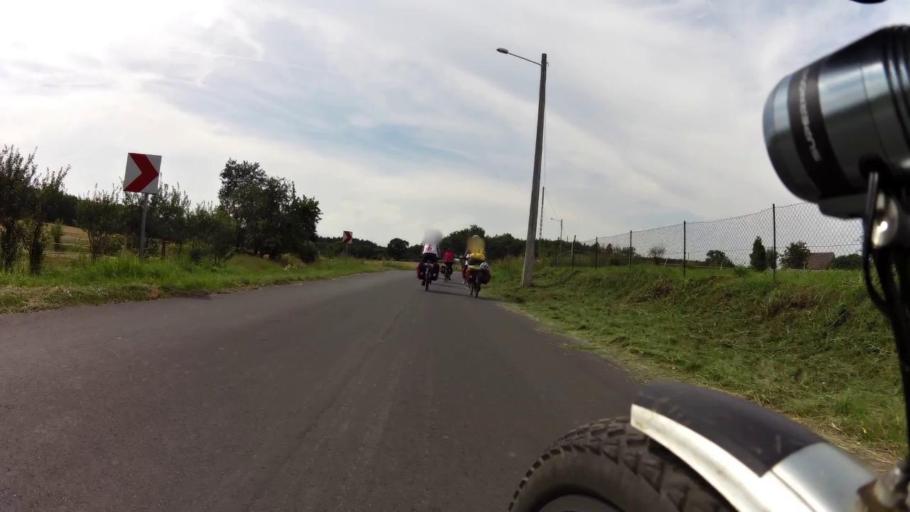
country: PL
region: West Pomeranian Voivodeship
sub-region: Powiat mysliborski
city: Debno
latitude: 52.7867
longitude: 14.6905
